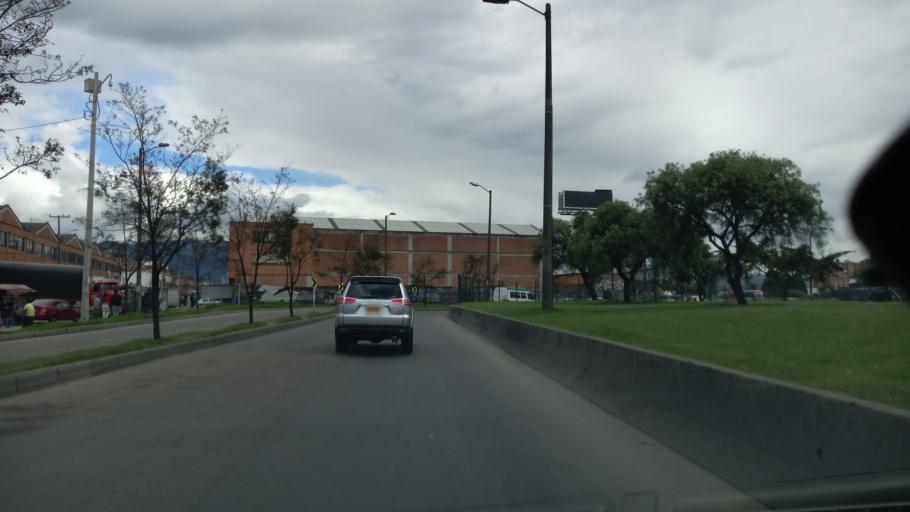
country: CO
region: Bogota D.C.
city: Bogota
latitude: 4.6489
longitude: -74.1257
